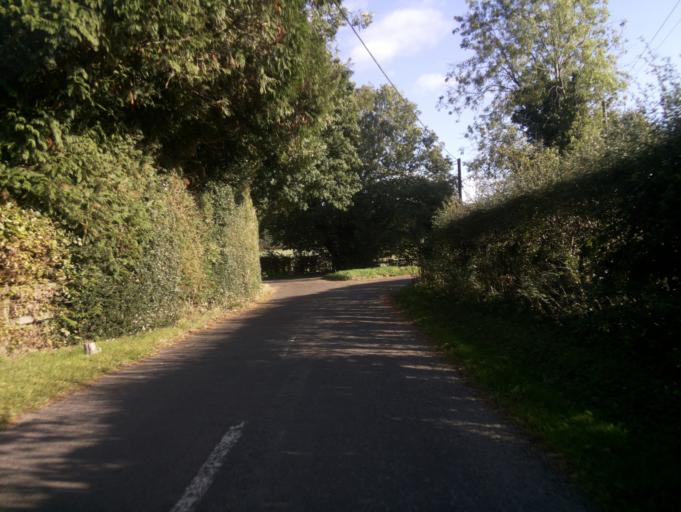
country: GB
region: England
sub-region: Hampshire
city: Four Marks
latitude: 51.0472
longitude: -1.0342
